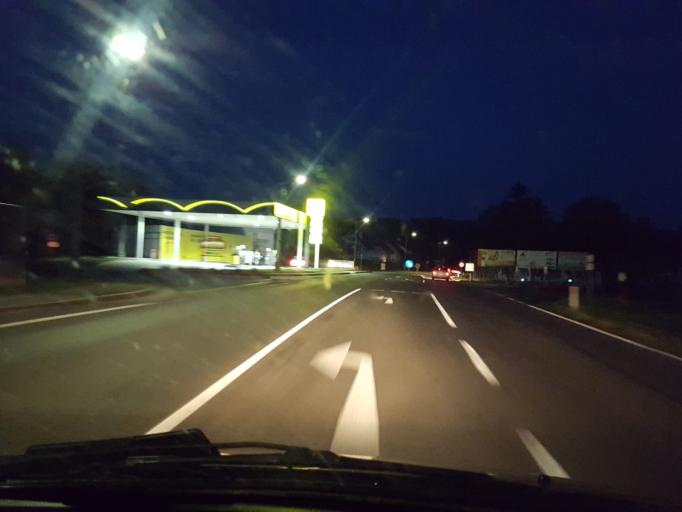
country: AT
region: Lower Austria
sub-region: Politischer Bezirk Scheibbs
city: Purgstall
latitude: 48.0626
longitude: 15.1385
